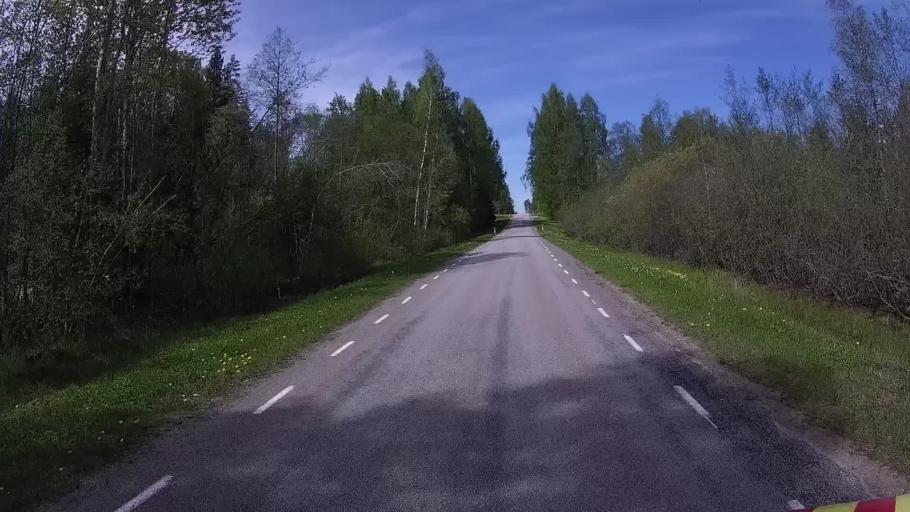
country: EE
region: Vorumaa
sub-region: Antsla vald
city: Vana-Antsla
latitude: 57.6237
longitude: 26.3473
